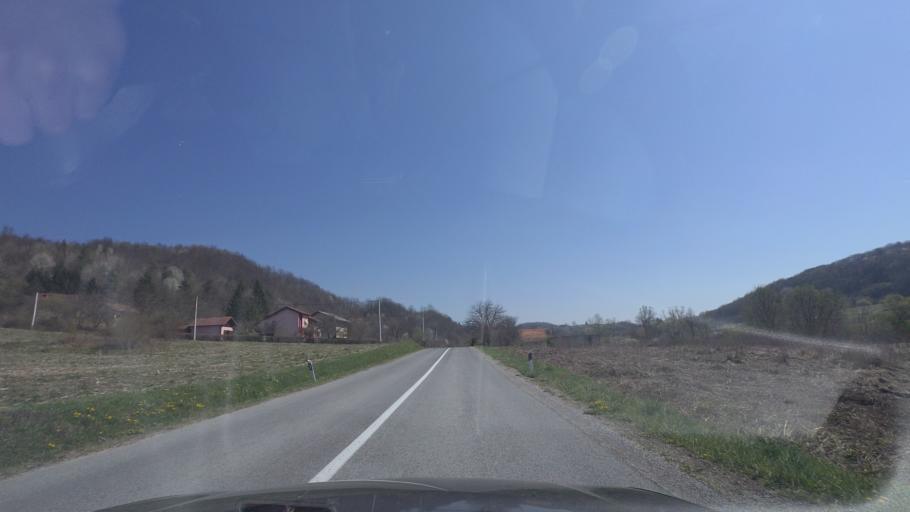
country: HR
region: Karlovacka
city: Vojnic
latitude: 45.3776
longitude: 15.6443
